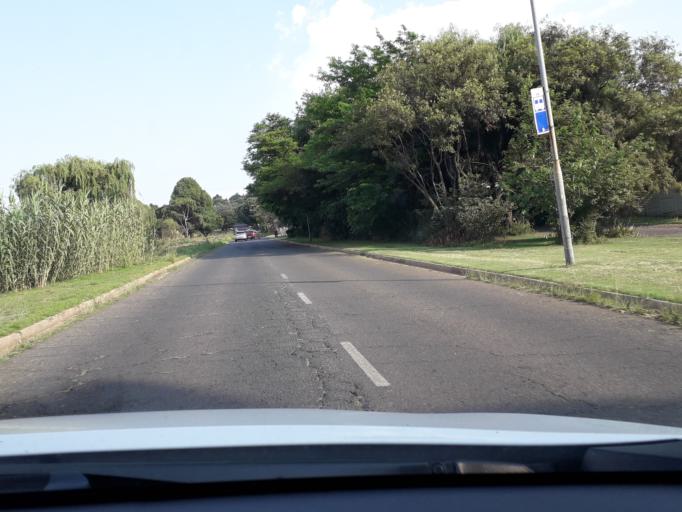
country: ZA
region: Gauteng
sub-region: City of Johannesburg Metropolitan Municipality
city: Johannesburg
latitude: -26.1580
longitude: 27.9743
